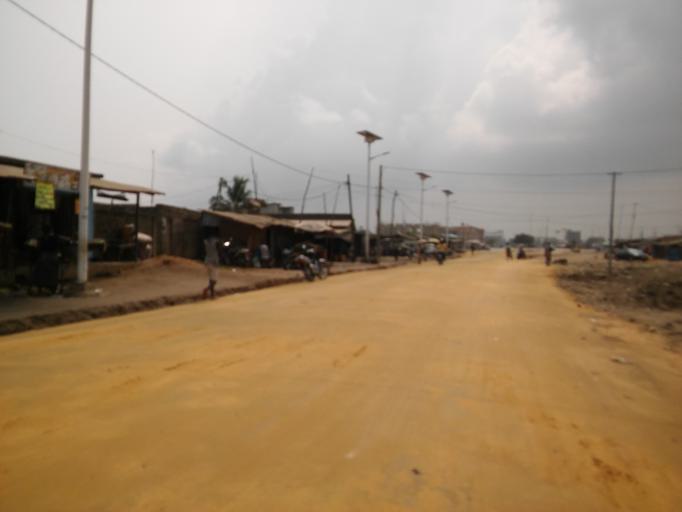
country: BJ
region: Littoral
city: Cotonou
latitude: 6.3903
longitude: 2.4115
